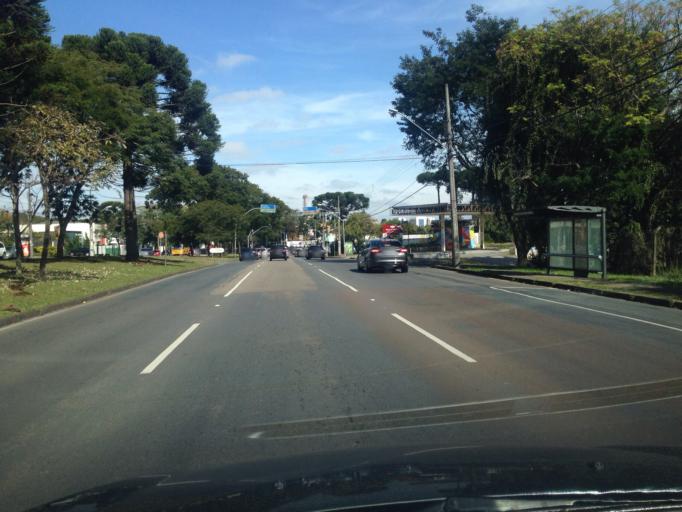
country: BR
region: Parana
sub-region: Curitiba
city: Curitiba
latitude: -25.4224
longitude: -49.2411
